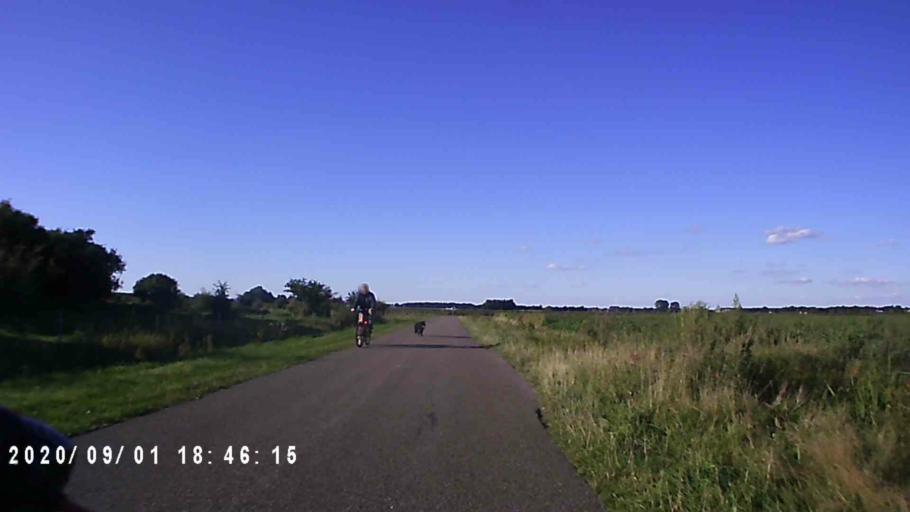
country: NL
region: Groningen
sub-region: Gemeente Veendam
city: Veendam
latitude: 53.1470
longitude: 6.8474
